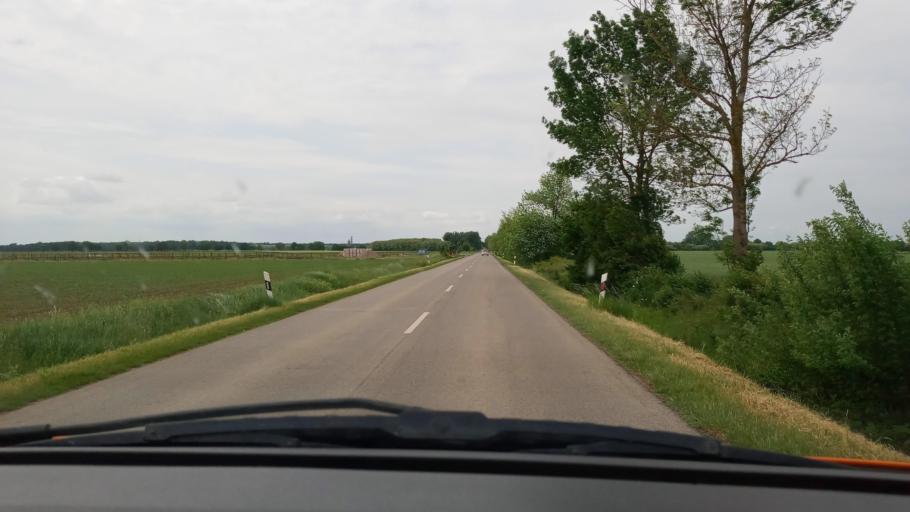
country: HU
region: Baranya
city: Vajszlo
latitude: 45.9143
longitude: 18.0527
